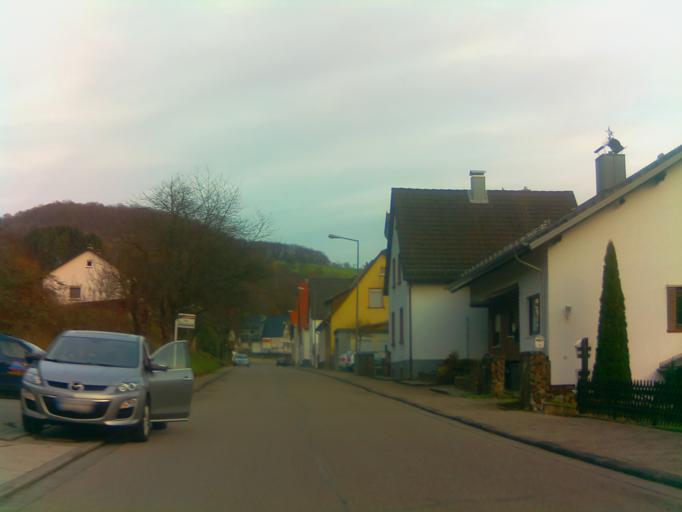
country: DE
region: Hesse
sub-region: Regierungsbezirk Darmstadt
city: Morlenbach
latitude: 49.5810
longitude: 8.7493
